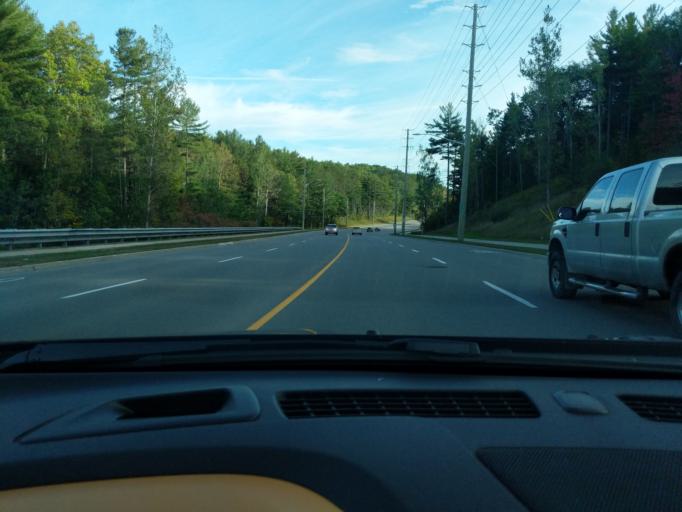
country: CA
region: Ontario
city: Barrie
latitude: 44.3888
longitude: -79.7318
